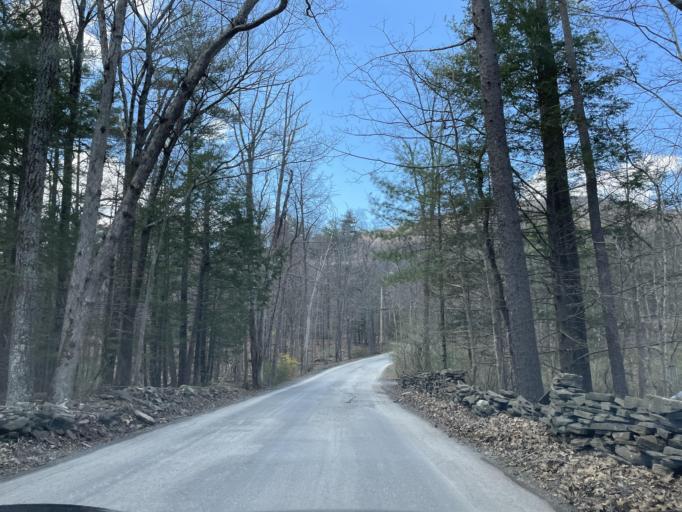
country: US
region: New York
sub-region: Ulster County
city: Zena
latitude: 42.0680
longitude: -74.0701
